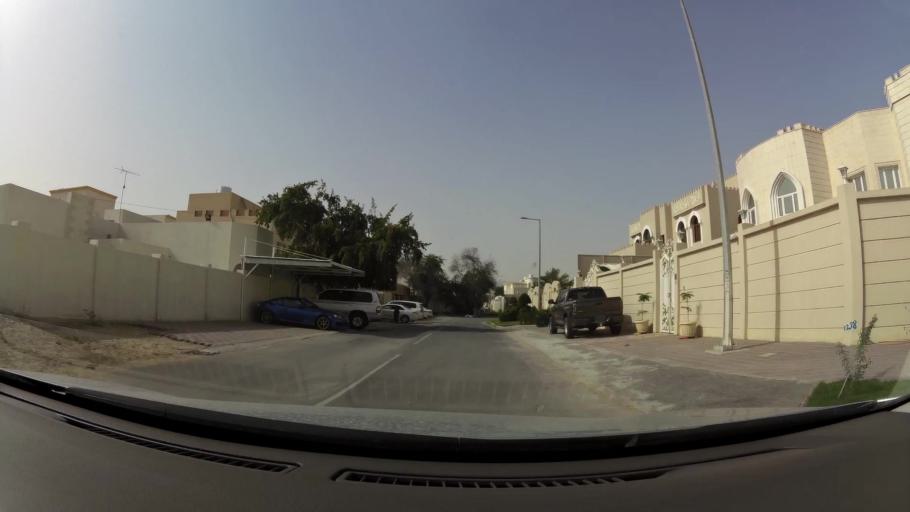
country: QA
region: Baladiyat ar Rayyan
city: Ar Rayyan
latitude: 25.2464
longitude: 51.4418
